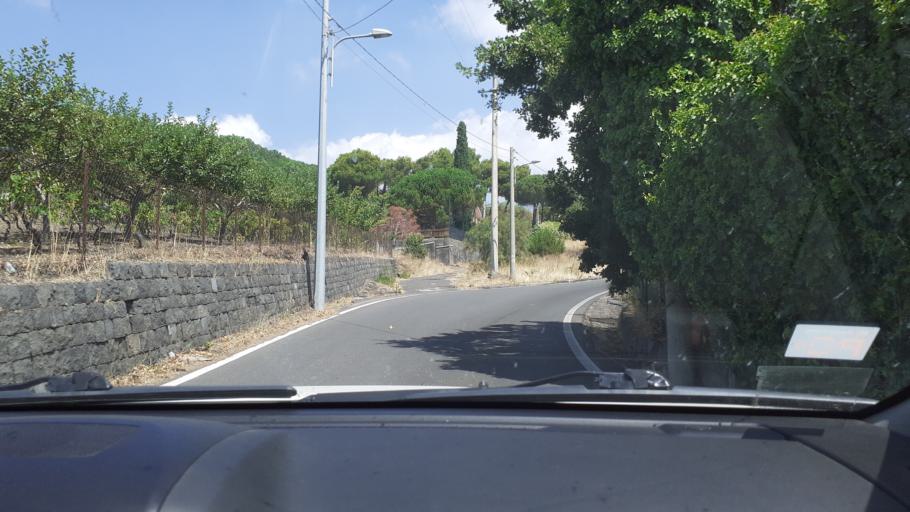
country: IT
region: Sicily
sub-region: Catania
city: Nicolosi
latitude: 37.6329
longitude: 15.0250
